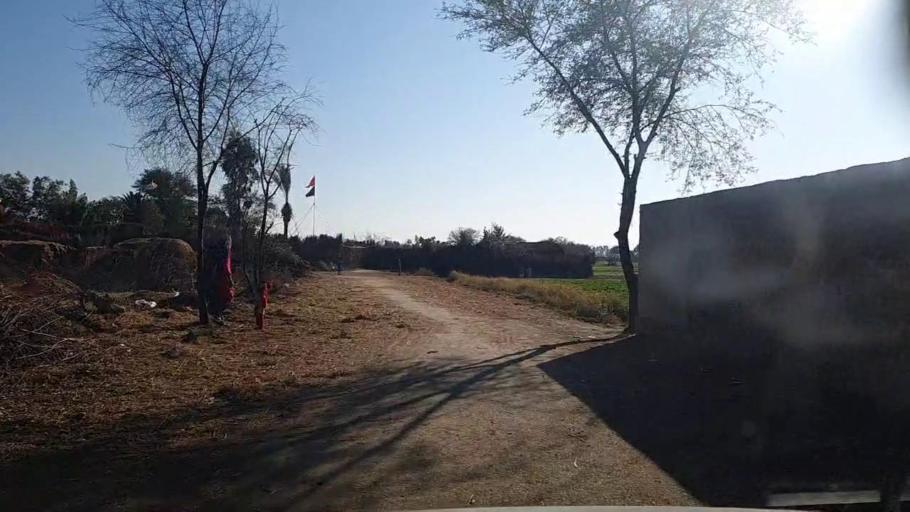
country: PK
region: Sindh
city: Khairpur
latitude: 27.9793
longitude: 69.7680
